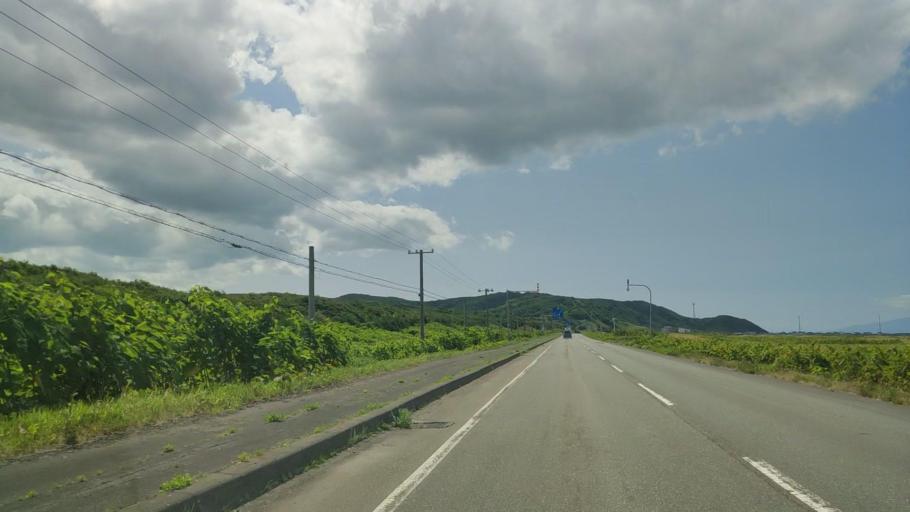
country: JP
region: Hokkaido
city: Wakkanai
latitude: 45.3203
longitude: 141.6377
